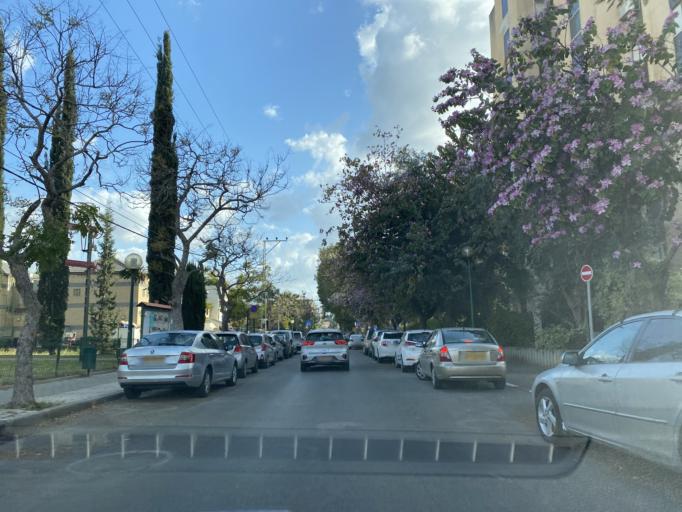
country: IL
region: Central District
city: Kfar Saba
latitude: 32.1796
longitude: 34.9188
